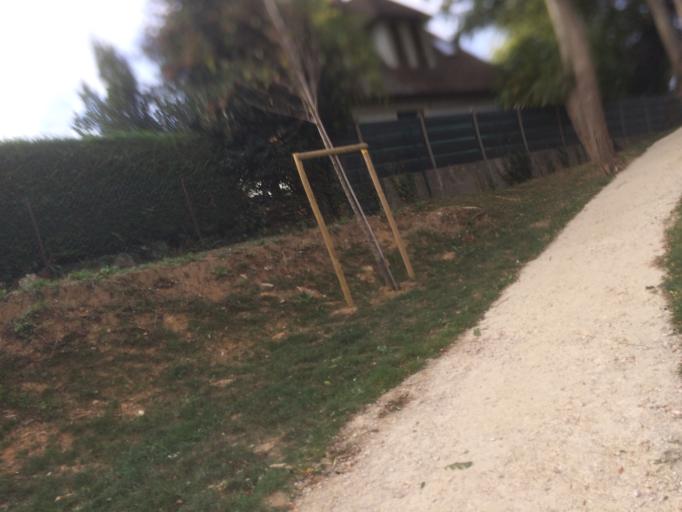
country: FR
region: Ile-de-France
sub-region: Departement de l'Essonne
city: Gometz-le-Chatel
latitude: 48.6744
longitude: 2.1433
